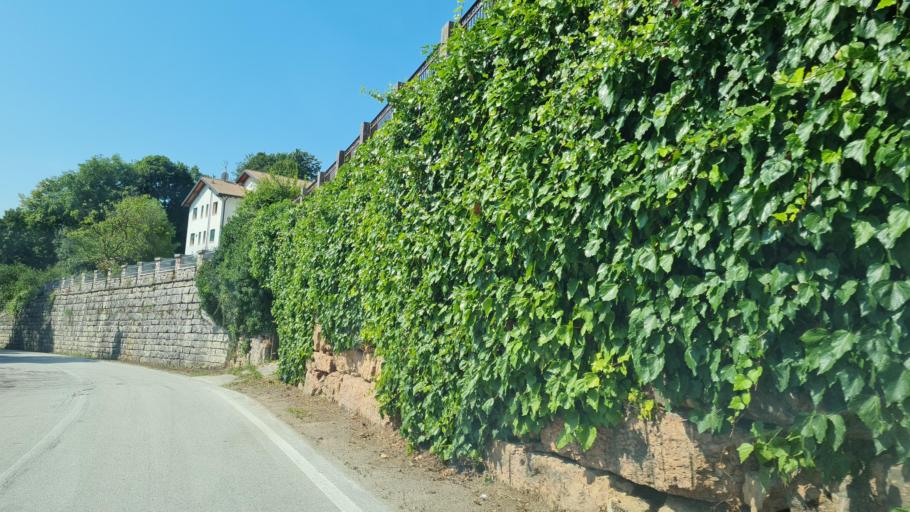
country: IT
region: Veneto
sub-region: Provincia di Vicenza
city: Conco
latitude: 45.7942
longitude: 11.6290
